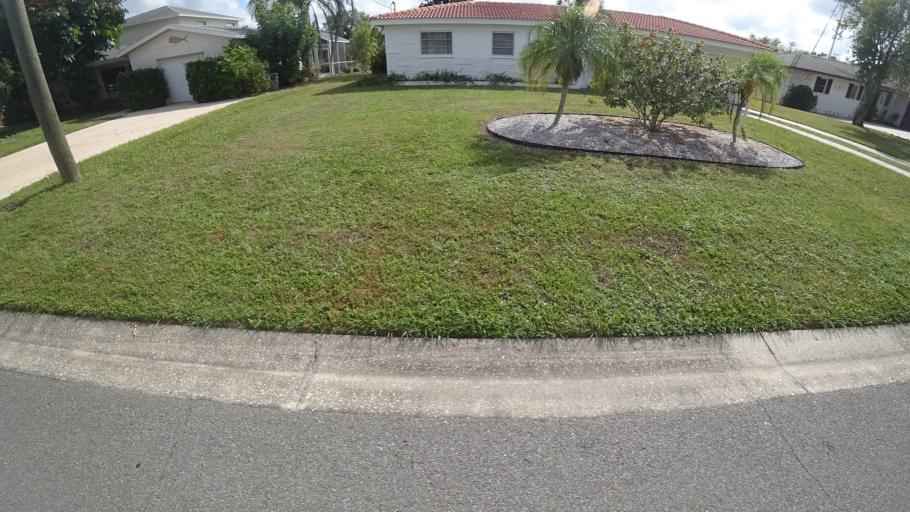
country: US
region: Florida
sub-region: Manatee County
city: Memphis
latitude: 27.5588
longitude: -82.5717
